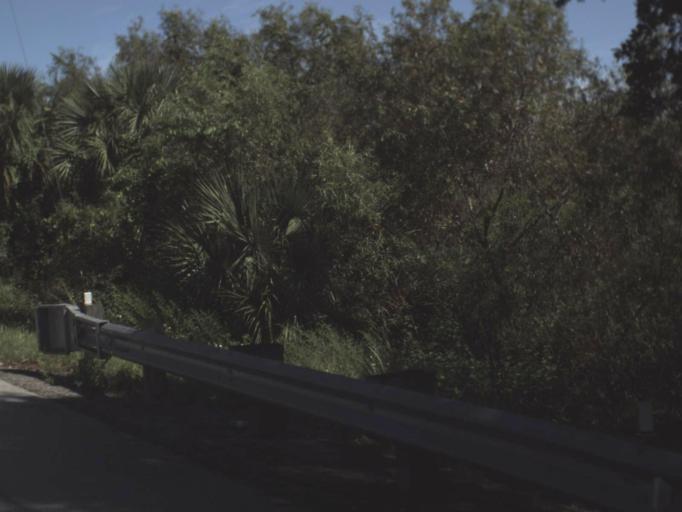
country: US
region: Florida
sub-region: Polk County
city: Polk City
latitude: 28.1365
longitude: -81.7951
